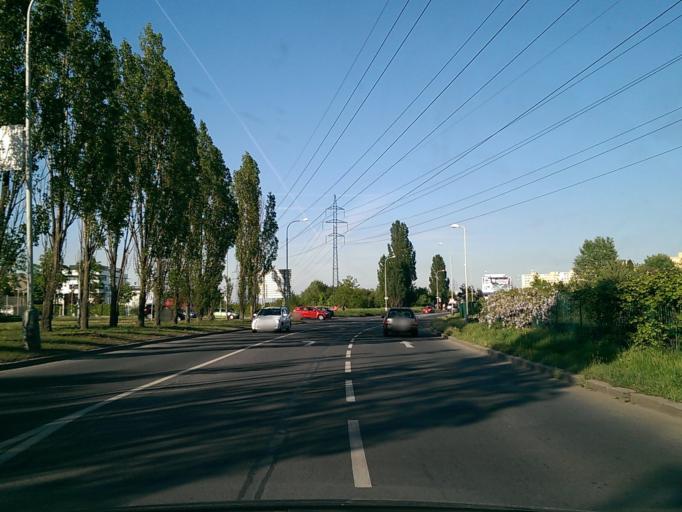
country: CZ
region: Central Bohemia
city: Vestec
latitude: 50.0373
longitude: 14.4968
